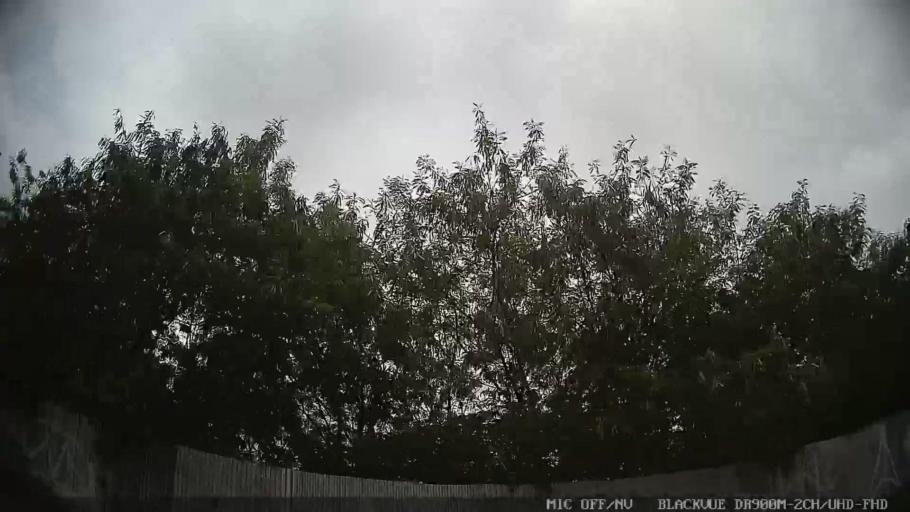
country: BR
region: Sao Paulo
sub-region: Osasco
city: Osasco
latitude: -23.4878
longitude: -46.7868
